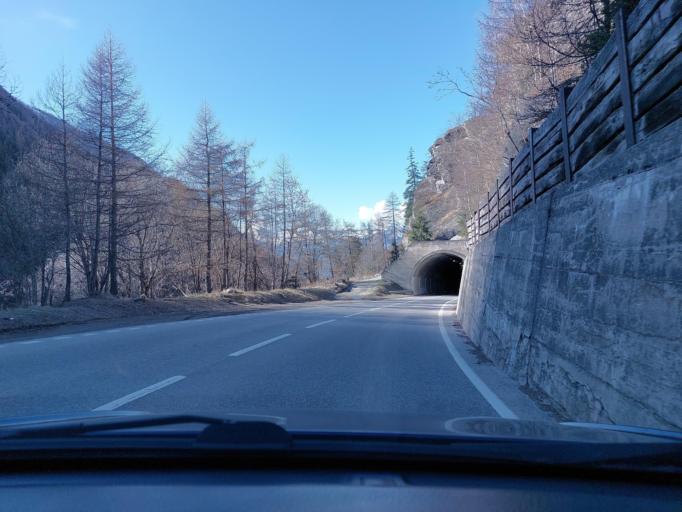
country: CH
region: Valais
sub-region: Herens District
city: Evolene
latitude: 46.1280
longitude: 7.4760
